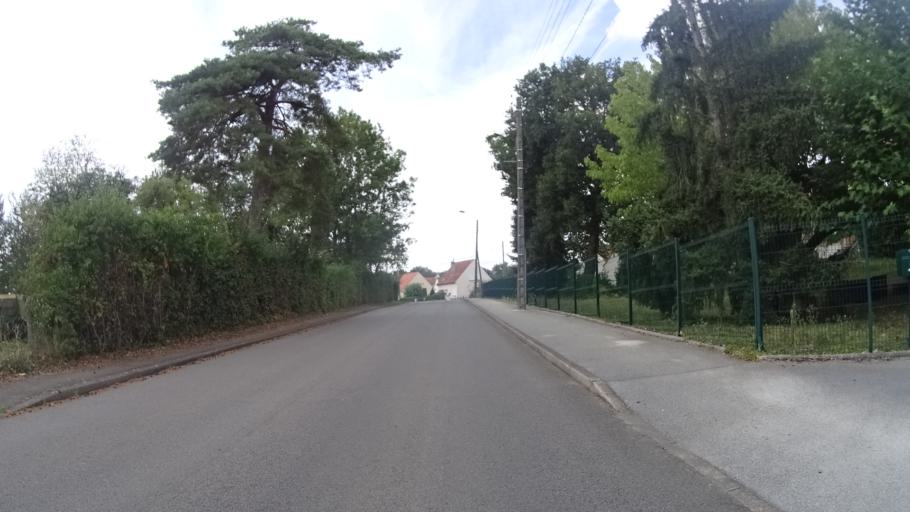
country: FR
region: Franche-Comte
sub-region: Departement du Jura
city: Damparis
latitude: 47.0749
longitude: 5.4090
